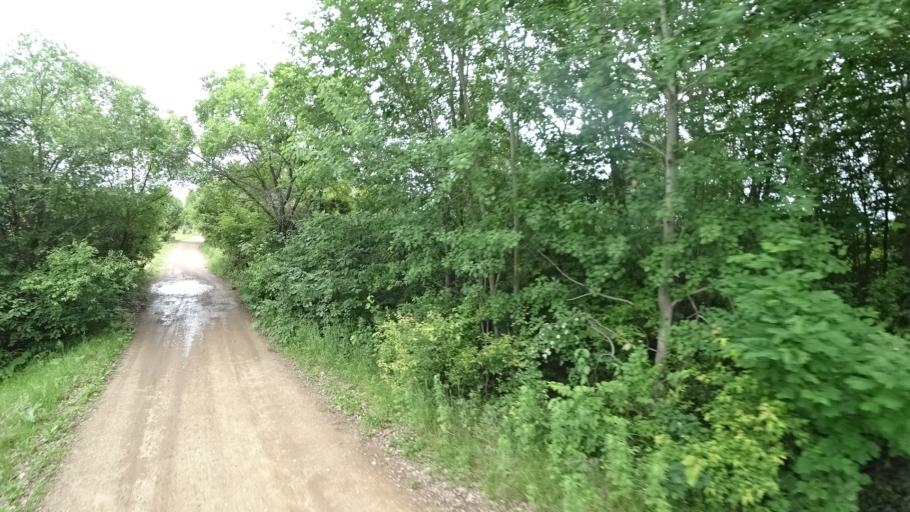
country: RU
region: Primorskiy
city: Arsen'yev
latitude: 44.1896
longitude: 133.3070
